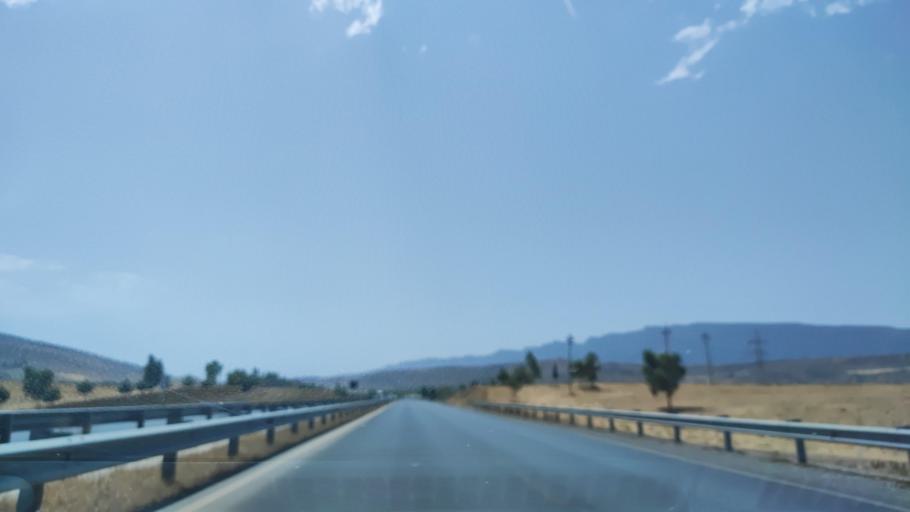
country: IQ
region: Arbil
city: Shaqlawah
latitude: 36.4641
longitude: 44.3832
